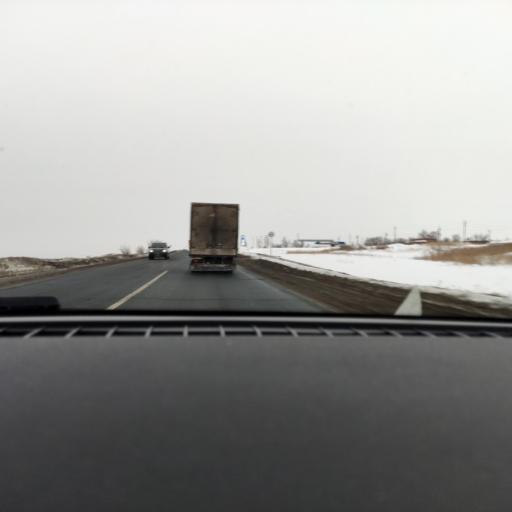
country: RU
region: Samara
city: Smyshlyayevka
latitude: 53.3027
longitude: 50.4584
